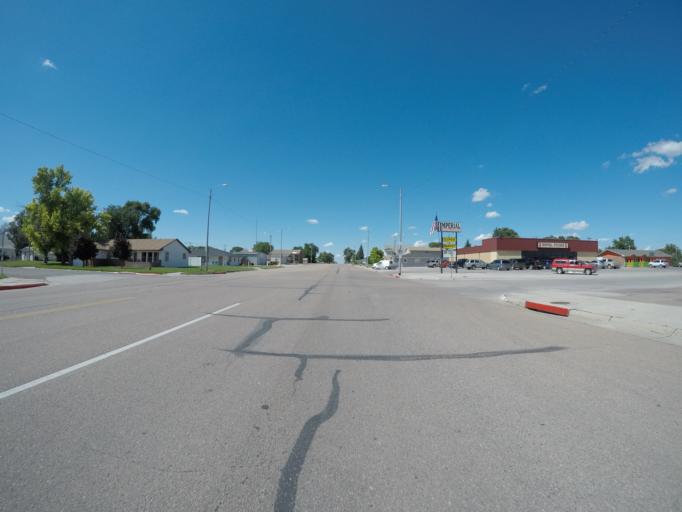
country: US
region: Nebraska
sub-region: Chase County
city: Imperial
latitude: 40.5231
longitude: -101.6431
